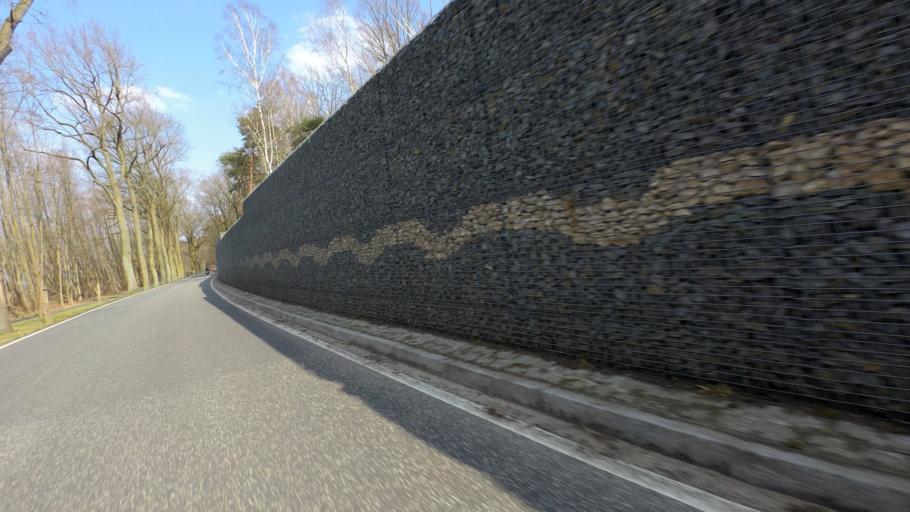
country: DE
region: Brandenburg
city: Werder
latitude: 52.3152
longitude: 12.9451
